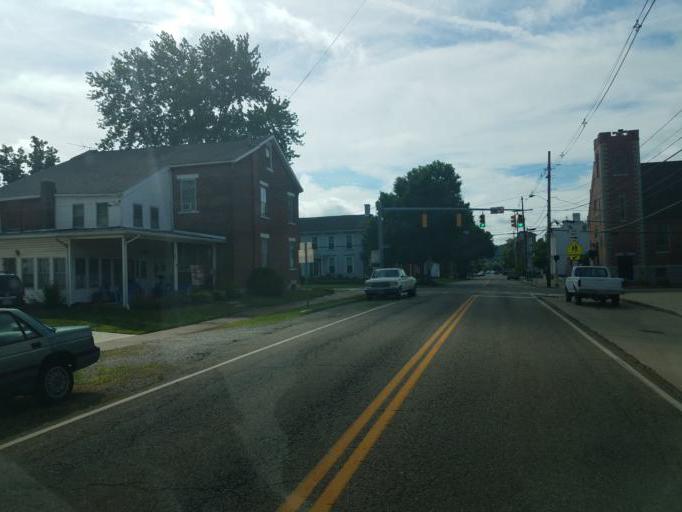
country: US
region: Ohio
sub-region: Gallia County
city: Gallipolis
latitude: 38.8100
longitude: -82.2075
